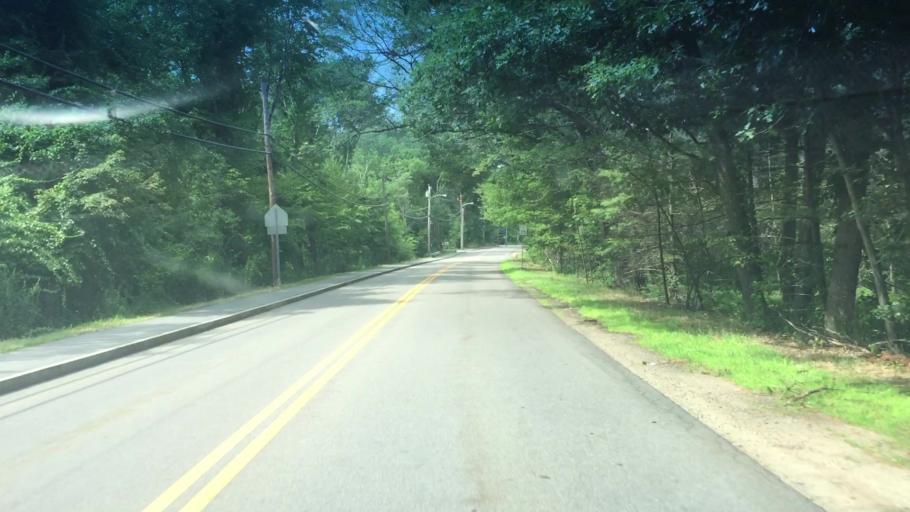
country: US
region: Massachusetts
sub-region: Norfolk County
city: Franklin
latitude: 42.1123
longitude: -71.3957
